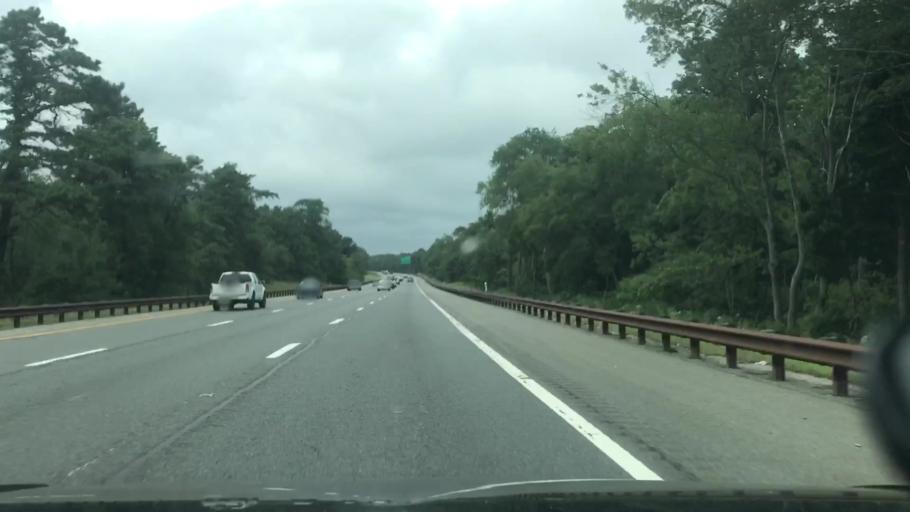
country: US
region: New Jersey
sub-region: Ocean County
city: Forked River
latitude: 39.8279
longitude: -74.2261
